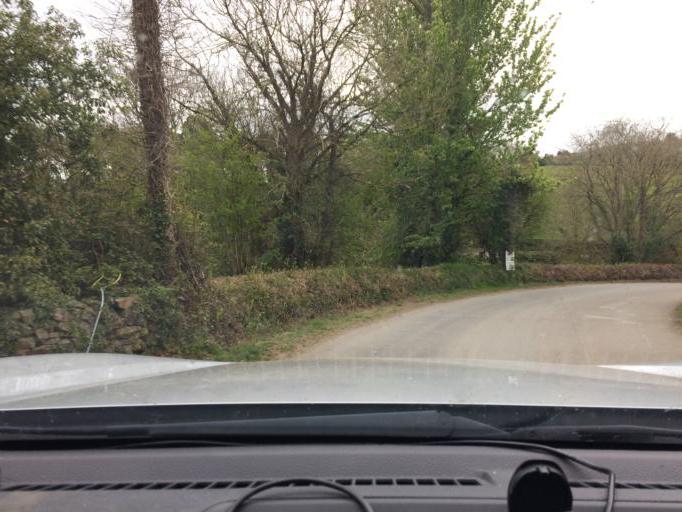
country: IE
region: Munster
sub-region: Waterford
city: Dungarvan
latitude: 52.0546
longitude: -7.6247
